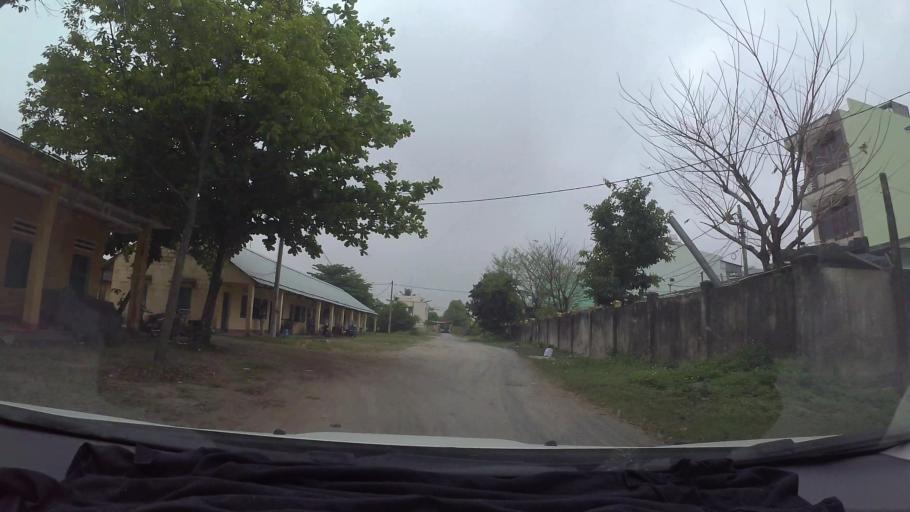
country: VN
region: Da Nang
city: Cam Le
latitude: 16.0412
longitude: 108.2069
